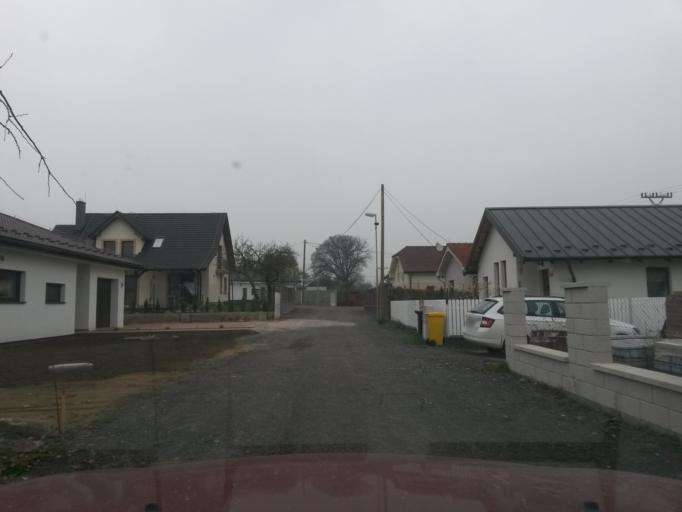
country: SK
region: Kosicky
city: Kosice
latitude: 48.8242
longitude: 21.3012
